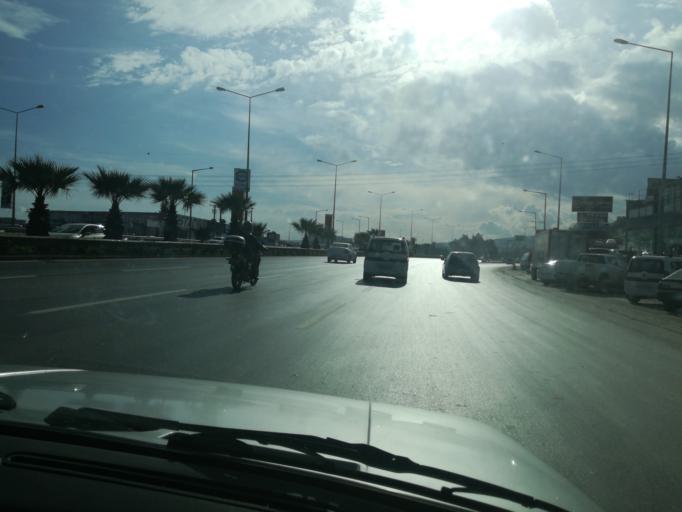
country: TR
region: Izmir
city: Karabaglar
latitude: 38.3505
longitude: 27.1334
